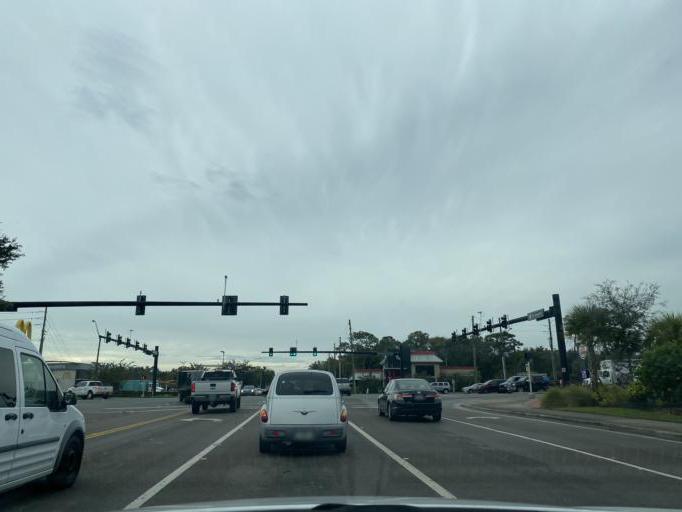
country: US
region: Florida
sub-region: Orange County
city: Winter Garden
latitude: 28.5516
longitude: -81.5835
